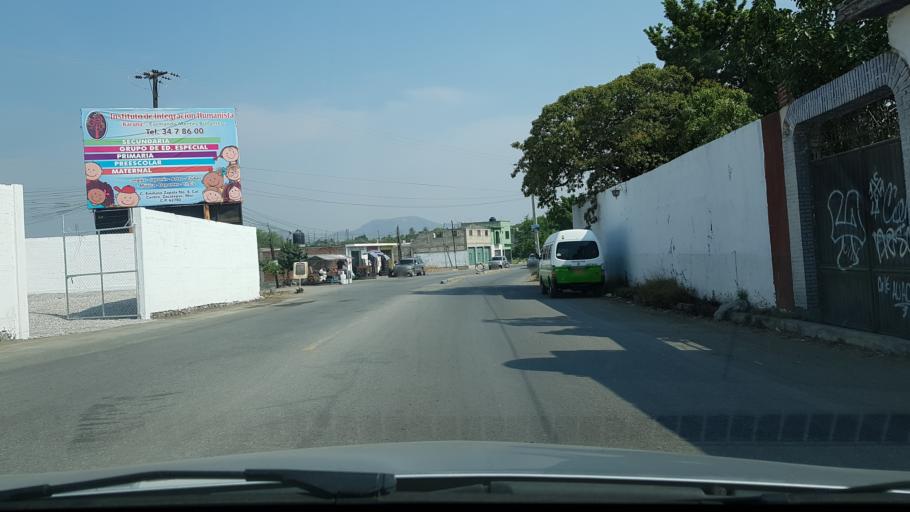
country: MX
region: Morelos
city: Zacatepec
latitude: 18.6650
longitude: -99.1862
